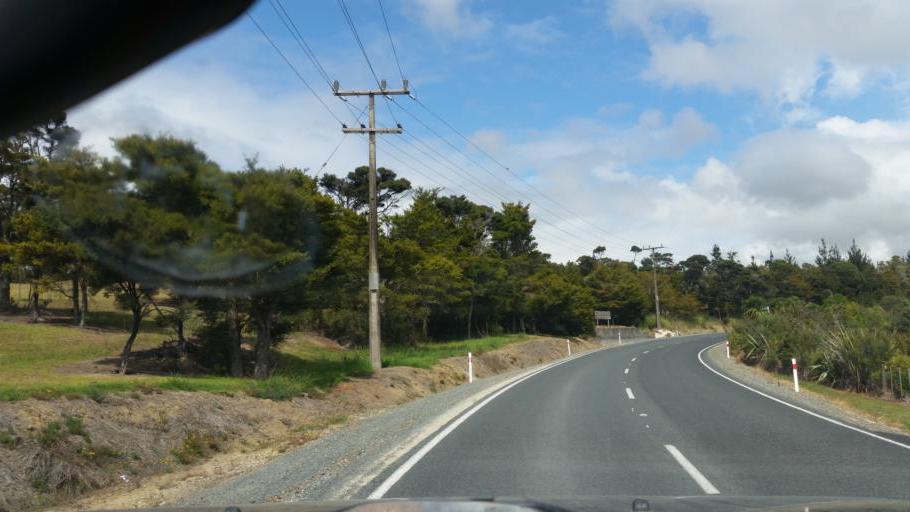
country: NZ
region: Auckland
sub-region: Auckland
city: Wellsford
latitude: -36.1124
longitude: 174.5448
